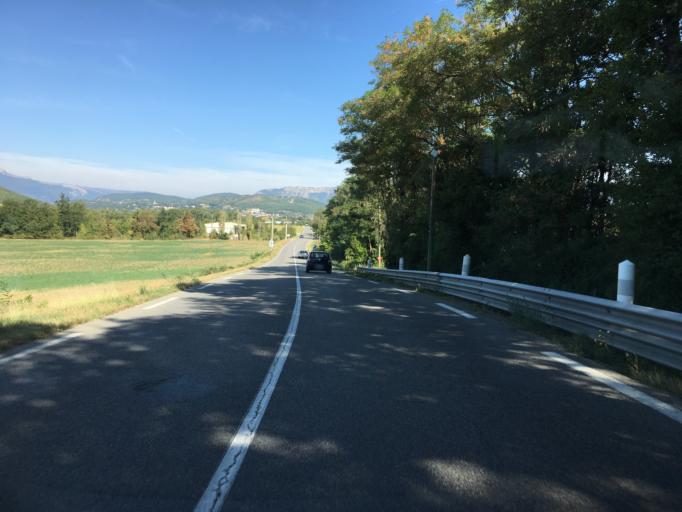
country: FR
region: Provence-Alpes-Cote d'Azur
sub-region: Departement des Hautes-Alpes
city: Laragne-Monteglin
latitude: 44.2919
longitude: 5.8432
